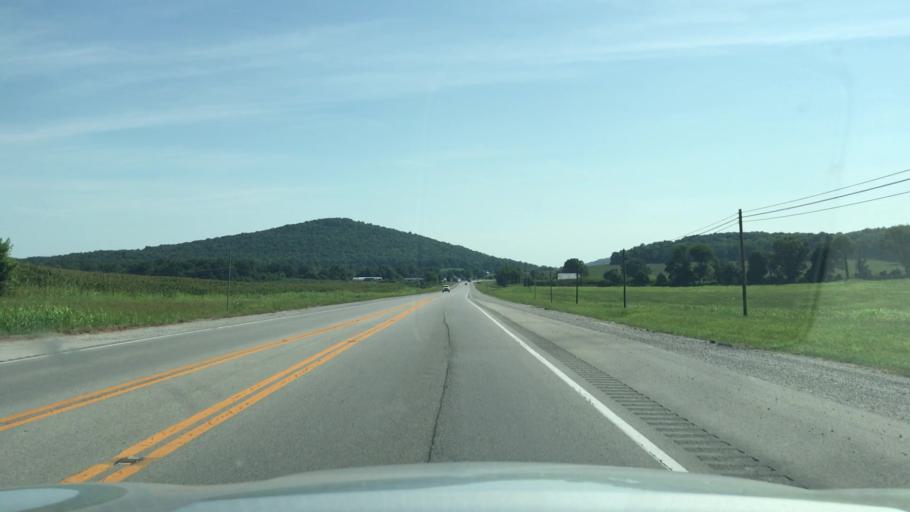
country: US
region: Kentucky
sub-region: Wayne County
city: Monticello
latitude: 36.7818
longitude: -84.9511
